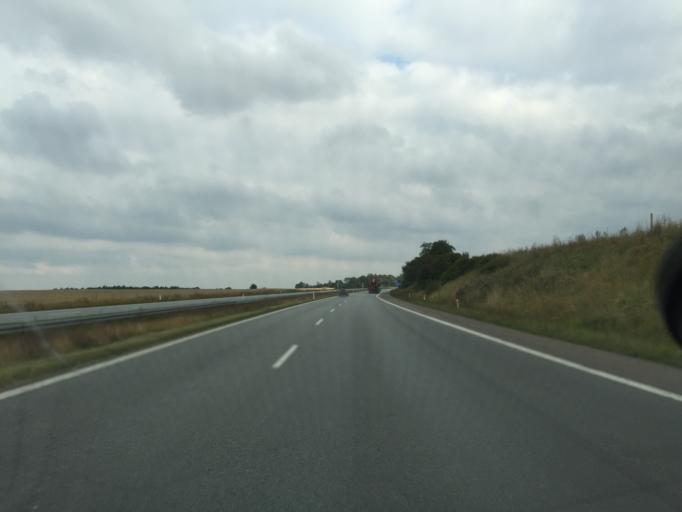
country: DK
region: Zealand
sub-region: Ringsted Kommune
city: Ringsted
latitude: 55.4559
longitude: 11.8347
